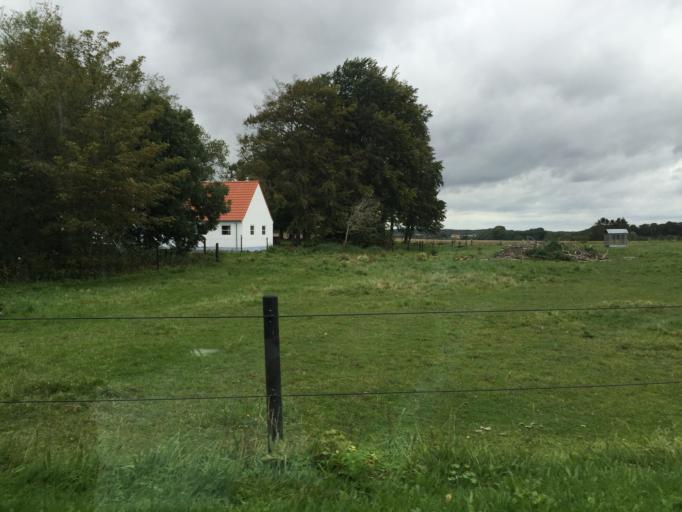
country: DK
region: South Denmark
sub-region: Kerteminde Kommune
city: Langeskov
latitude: 55.2260
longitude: 10.6079
